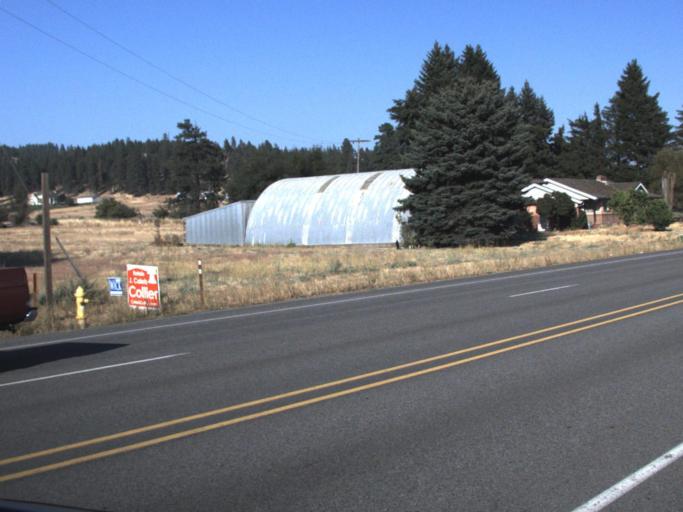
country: US
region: Washington
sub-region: Spokane County
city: Trentwood
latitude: 47.6969
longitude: -117.1715
